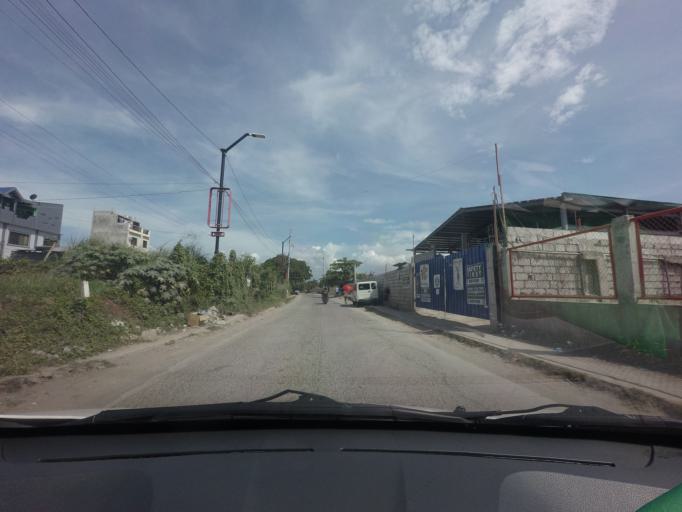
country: PH
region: Calabarzon
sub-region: Province of Rizal
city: Taguig
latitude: 14.5281
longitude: 121.0875
